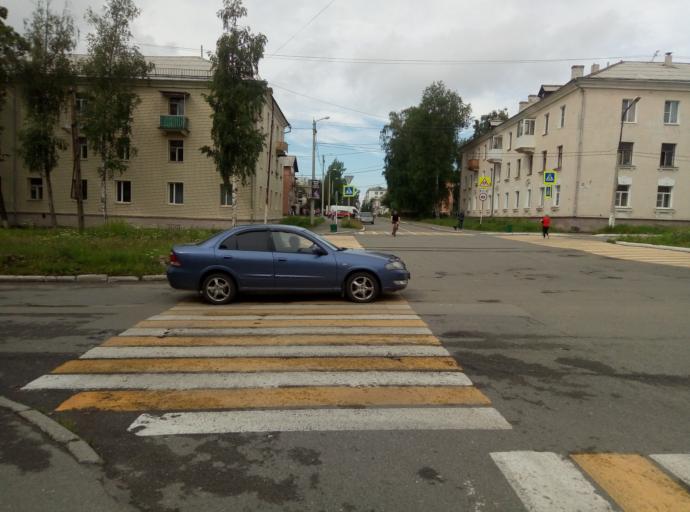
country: RU
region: Sverdlovsk
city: Krasnotur'insk
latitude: 59.7619
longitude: 60.1877
